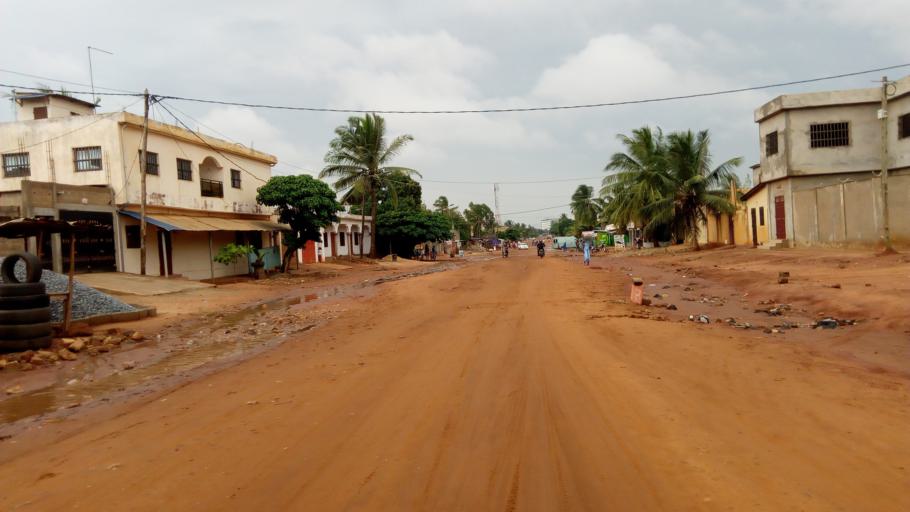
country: TG
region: Maritime
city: Lome
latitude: 6.2301
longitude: 1.1818
